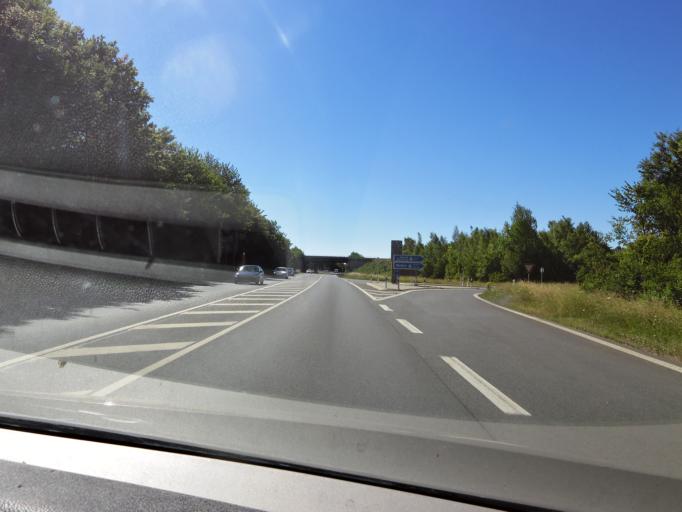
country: DE
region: Bavaria
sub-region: Regierungsbezirk Unterfranken
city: Biebelried
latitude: 49.7596
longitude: 10.1084
